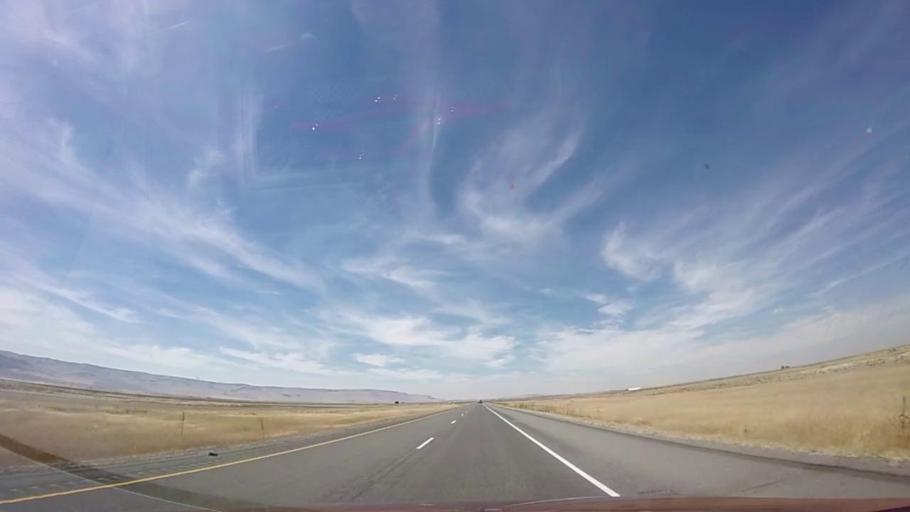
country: US
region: Idaho
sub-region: Minidoka County
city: Rupert
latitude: 42.4018
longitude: -113.3033
